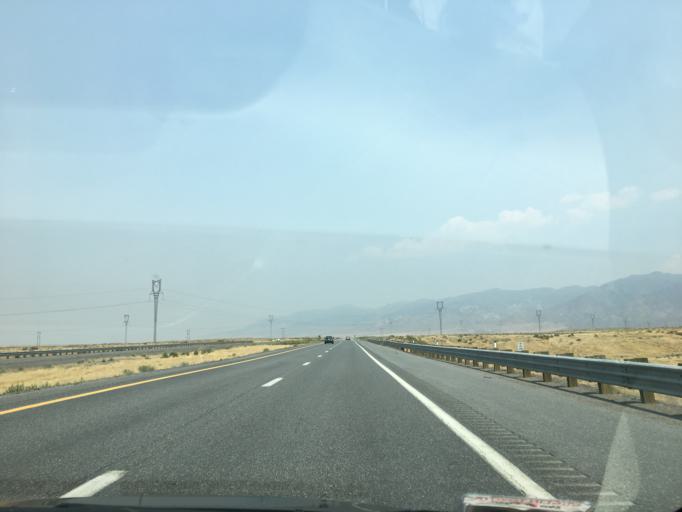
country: US
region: Nevada
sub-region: Pershing County
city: Lovelock
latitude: 40.3075
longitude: -118.3406
